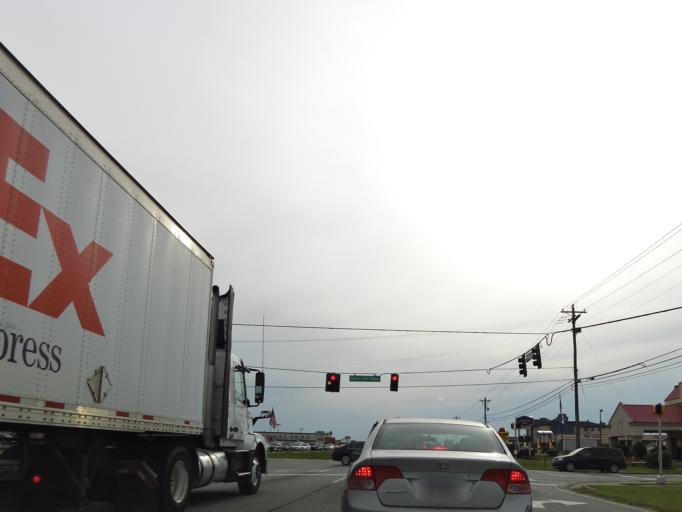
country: US
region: Georgia
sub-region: Houston County
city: Centerville
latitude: 32.6166
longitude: -83.6956
